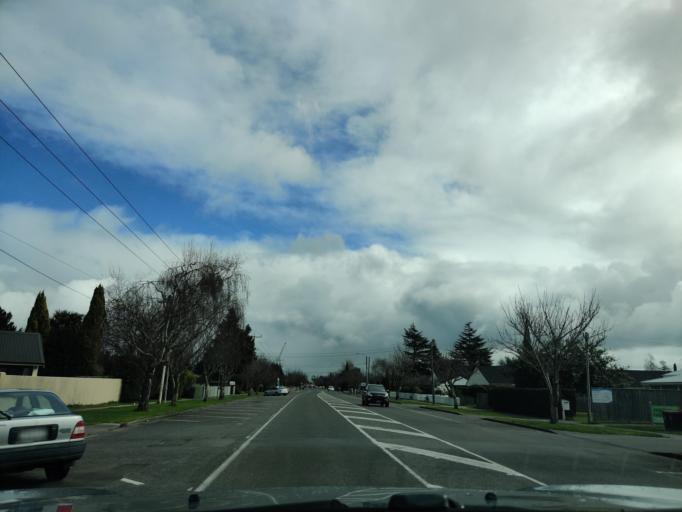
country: NZ
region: Hawke's Bay
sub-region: Hastings District
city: Hastings
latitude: -39.6707
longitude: 176.8749
